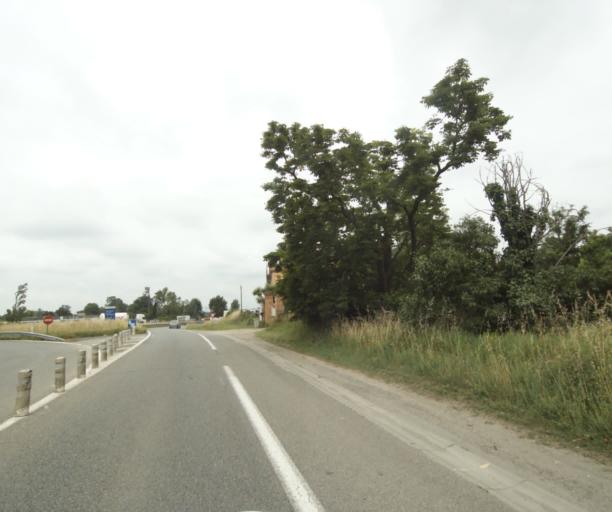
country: FR
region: Midi-Pyrenees
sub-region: Departement du Tarn-et-Garonne
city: Bressols
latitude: 43.9787
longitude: 1.3355
